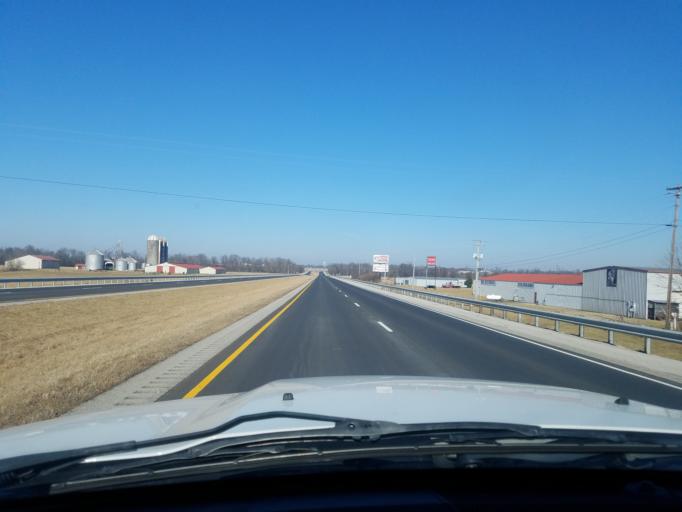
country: US
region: Kentucky
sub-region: Larue County
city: Hodgenville
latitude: 37.5696
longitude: -85.7504
